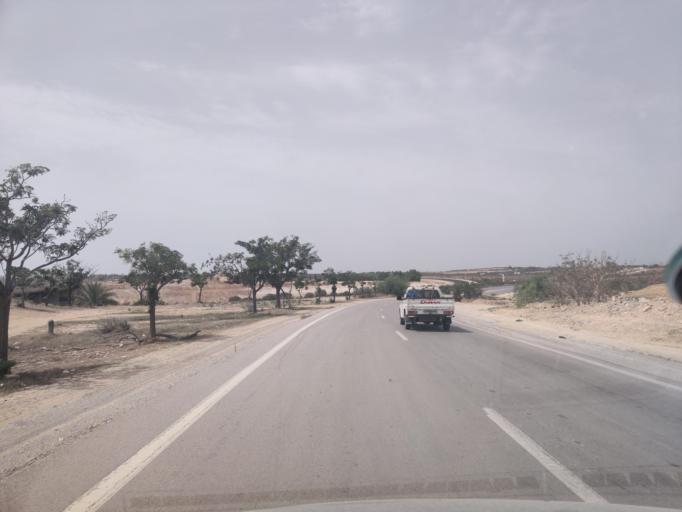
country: TN
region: Susah
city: Akouda
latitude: 35.8400
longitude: 10.5352
